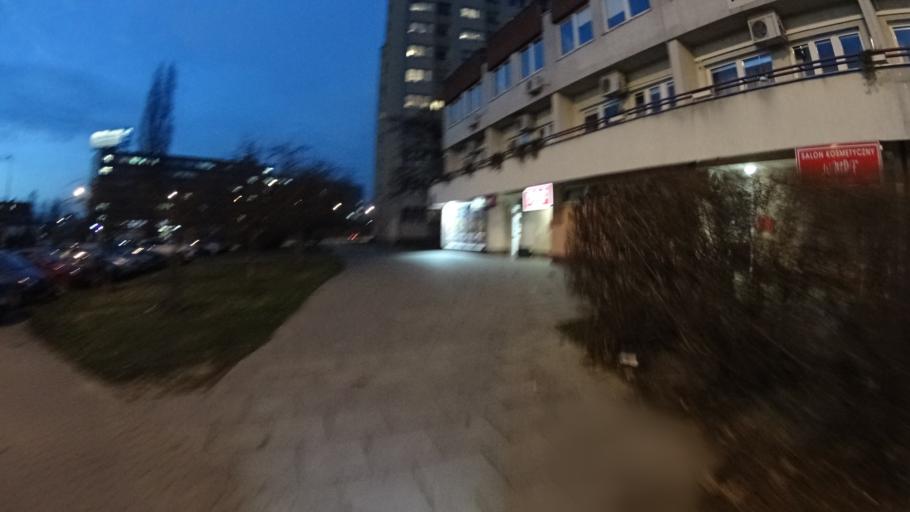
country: PL
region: Masovian Voivodeship
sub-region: Warszawa
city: Praga Poludnie
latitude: 52.2360
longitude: 21.0801
